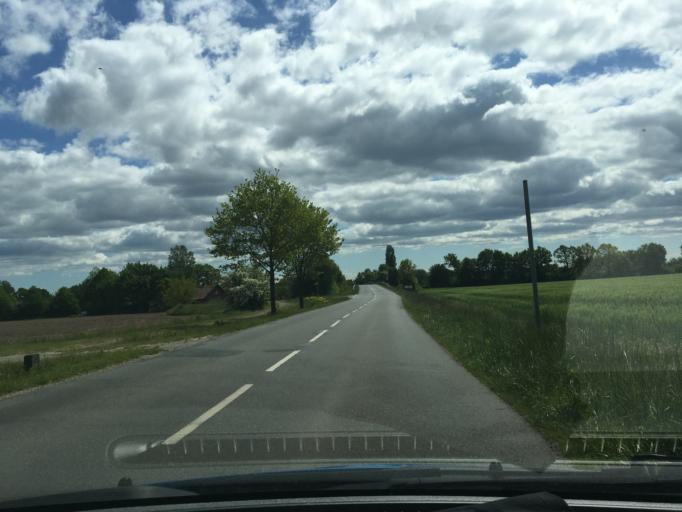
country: DE
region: Lower Saxony
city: Suderburg
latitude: 52.9329
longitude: 10.4851
